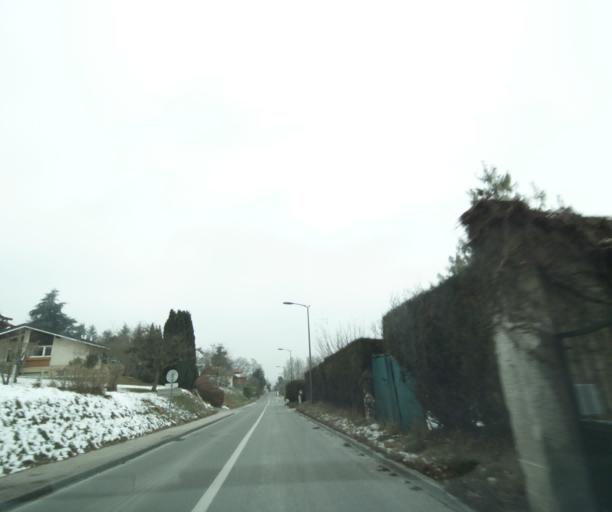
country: FR
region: Rhone-Alpes
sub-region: Departement de la Haute-Savoie
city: Vetraz-Monthoux
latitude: 46.1685
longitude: 6.2386
